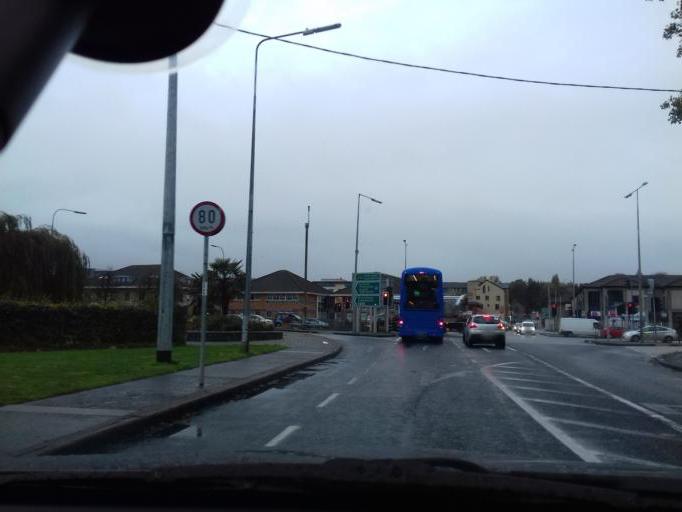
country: IE
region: Leinster
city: Oldbawn
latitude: 53.2855
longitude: -6.3613
